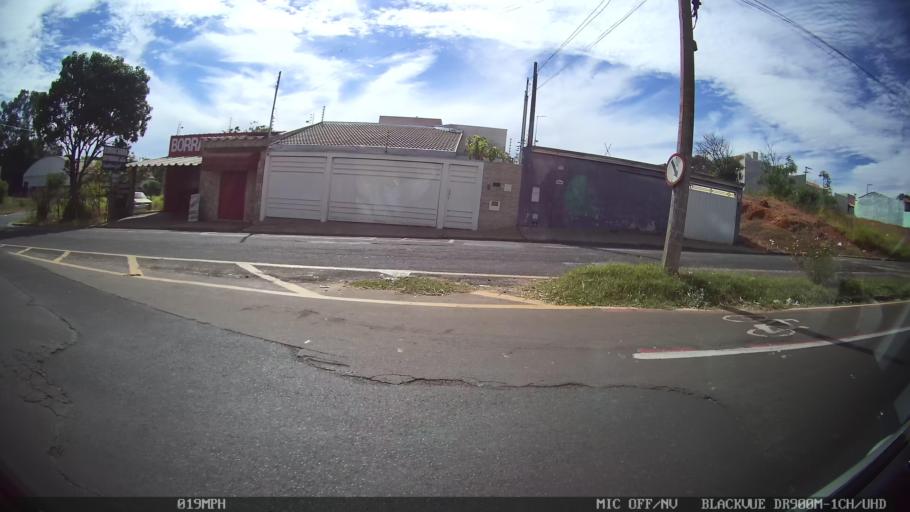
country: BR
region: Sao Paulo
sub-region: Catanduva
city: Catanduva
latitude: -21.1393
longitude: -48.9551
